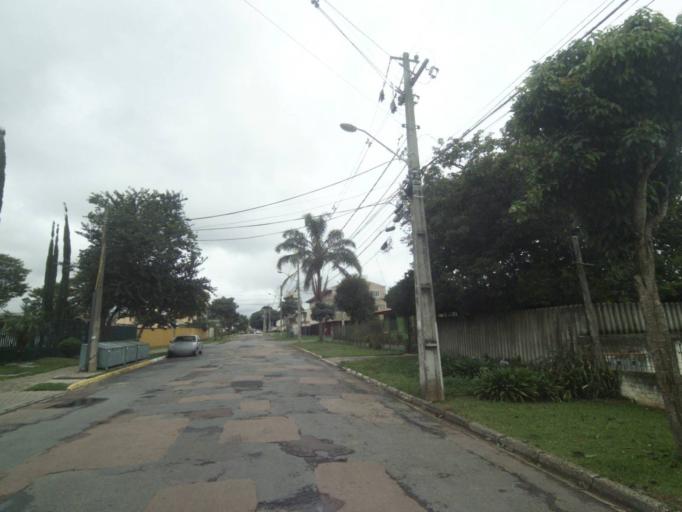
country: BR
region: Parana
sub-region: Curitiba
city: Curitiba
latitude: -25.4955
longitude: -49.3079
